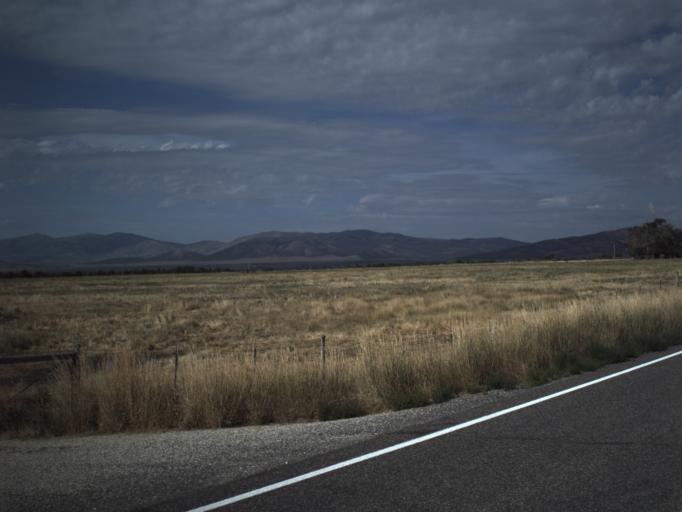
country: US
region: Idaho
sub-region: Cassia County
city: Burley
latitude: 41.8193
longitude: -113.4206
